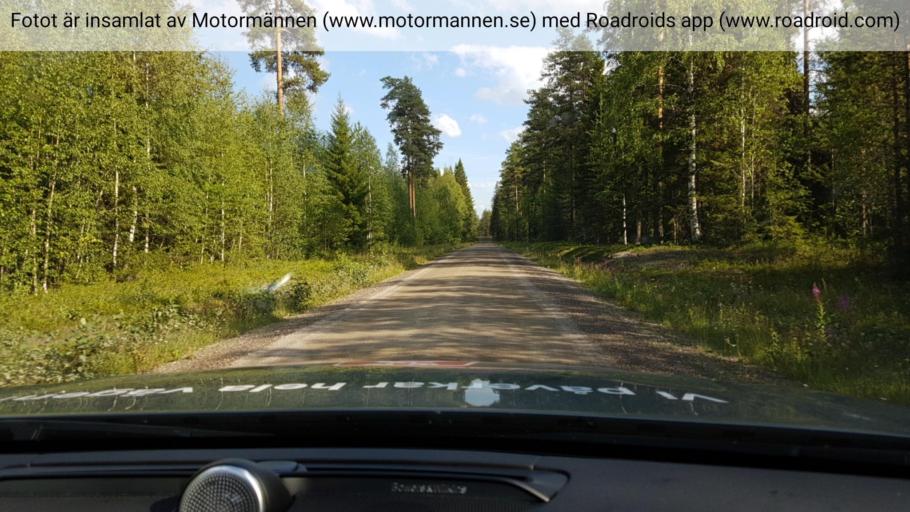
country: SE
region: Vaesterbotten
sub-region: Dorotea Kommun
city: Dorotea
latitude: 63.9772
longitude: 16.0455
